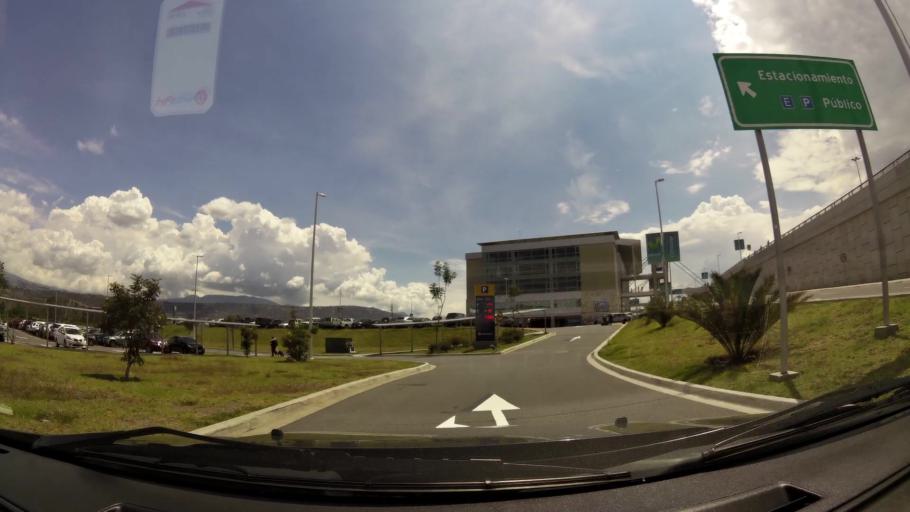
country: EC
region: Pichincha
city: Quito
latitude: -0.1258
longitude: -78.3611
